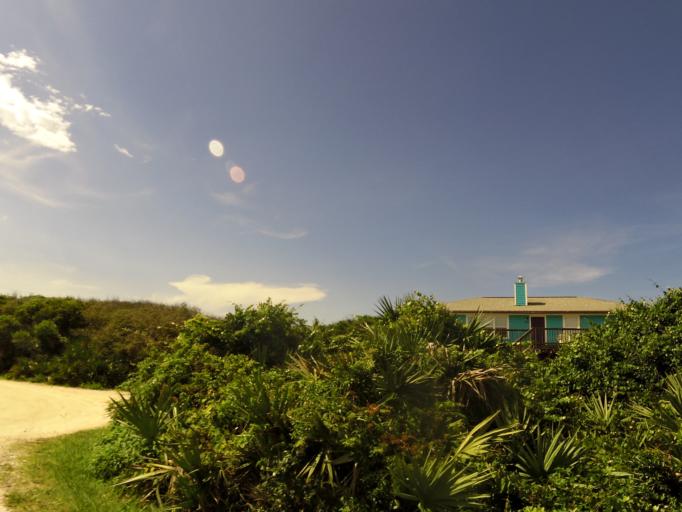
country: US
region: Florida
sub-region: Saint Johns County
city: Villano Beach
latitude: 30.0237
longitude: -81.3249
